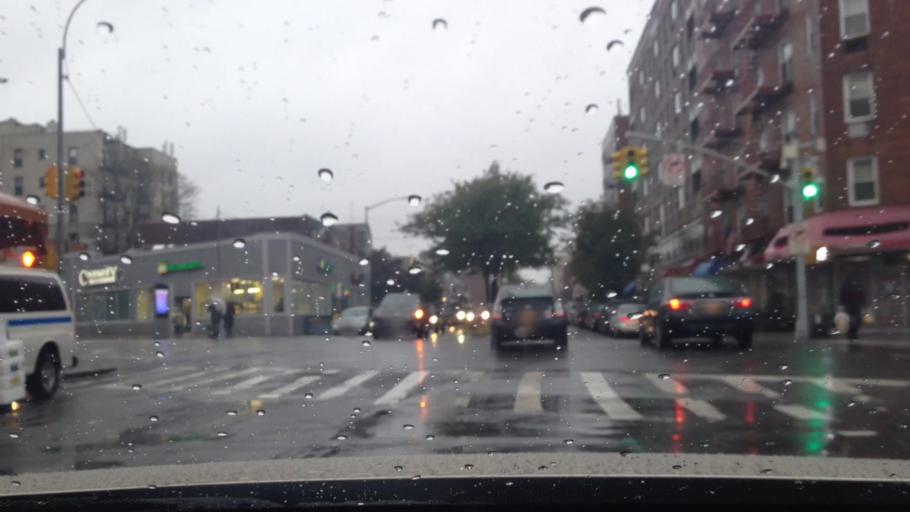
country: US
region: New York
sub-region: Queens County
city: Long Island City
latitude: 40.7465
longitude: -73.8904
